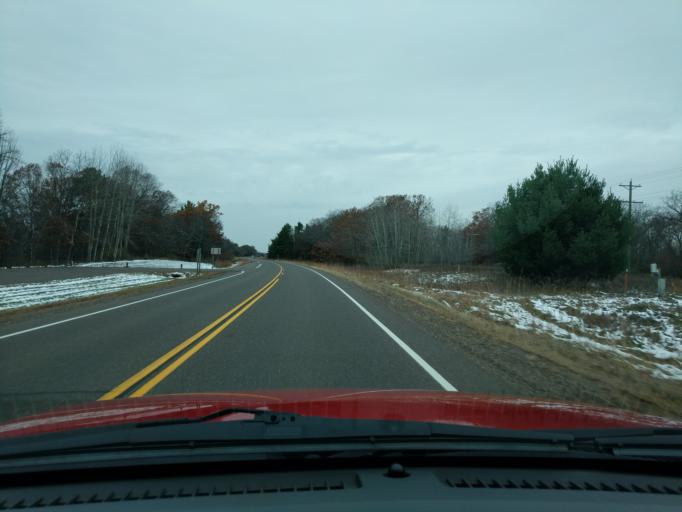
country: US
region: Wisconsin
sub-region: Burnett County
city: Siren
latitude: 45.8240
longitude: -92.2540
